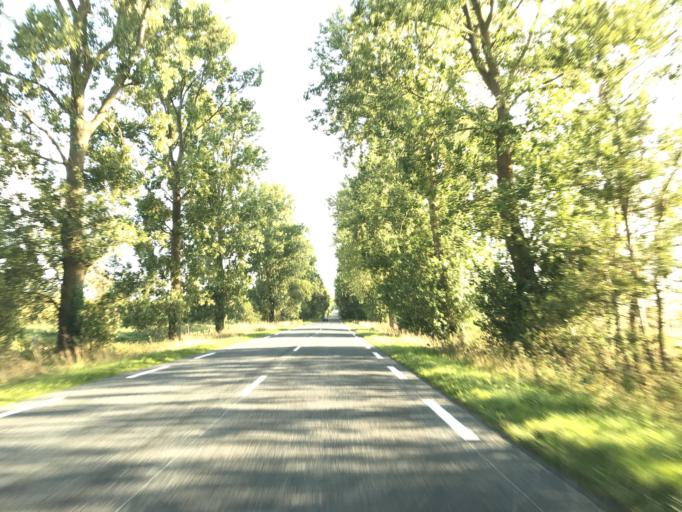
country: FR
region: Haute-Normandie
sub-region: Departement de la Seine-Maritime
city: La Remuee
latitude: 49.5236
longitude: 0.4202
